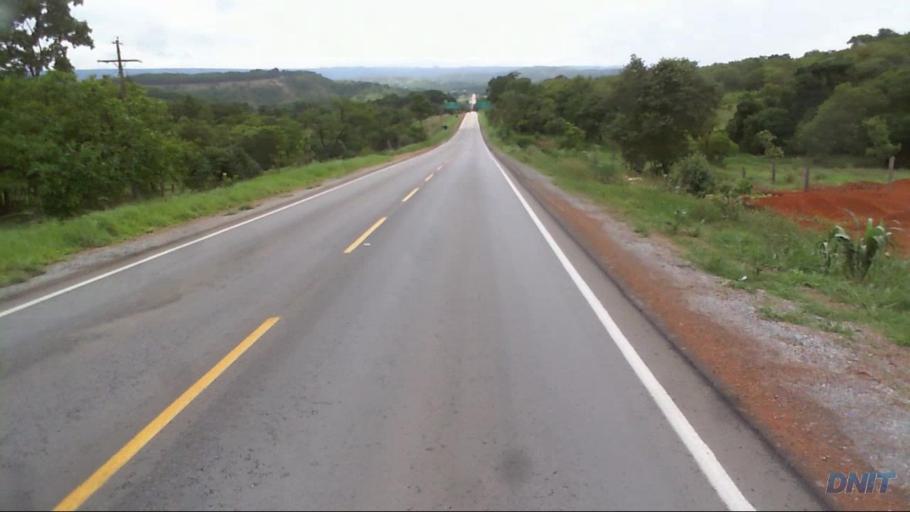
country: BR
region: Goias
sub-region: Padre Bernardo
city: Padre Bernardo
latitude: -15.5088
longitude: -48.1971
